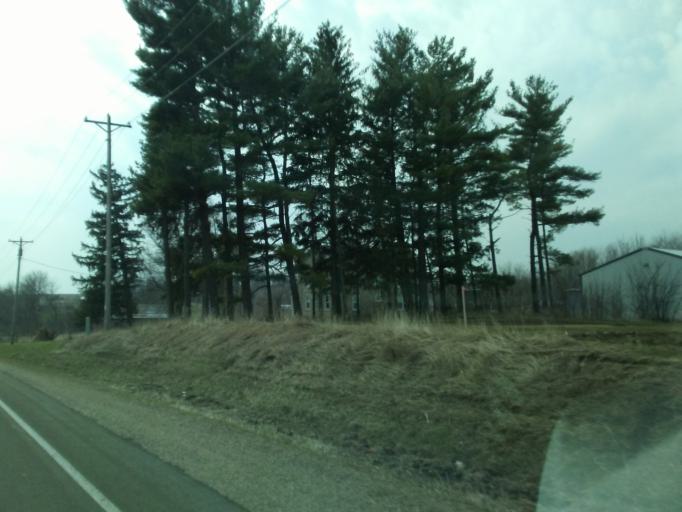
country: US
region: Wisconsin
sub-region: Dane County
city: Middleton
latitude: 43.1459
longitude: -89.4918
